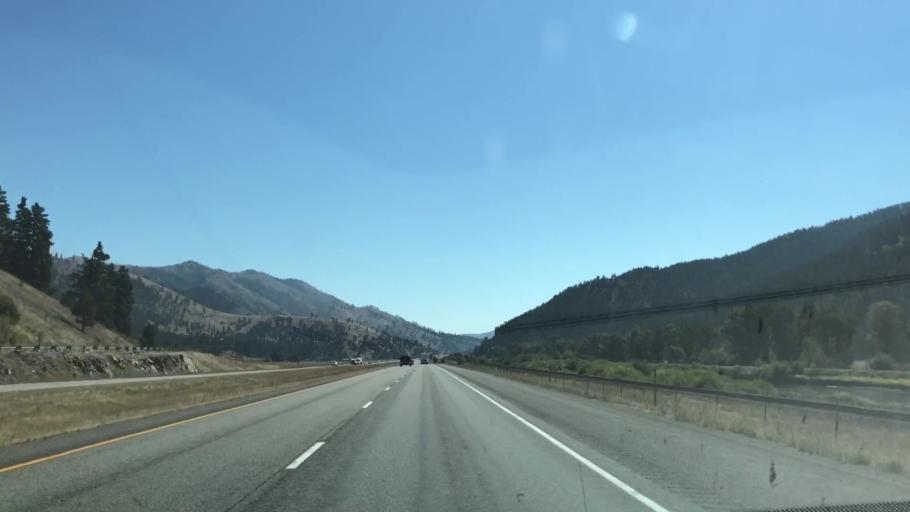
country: US
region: Montana
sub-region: Missoula County
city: Clinton
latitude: 46.7216
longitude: -113.5582
